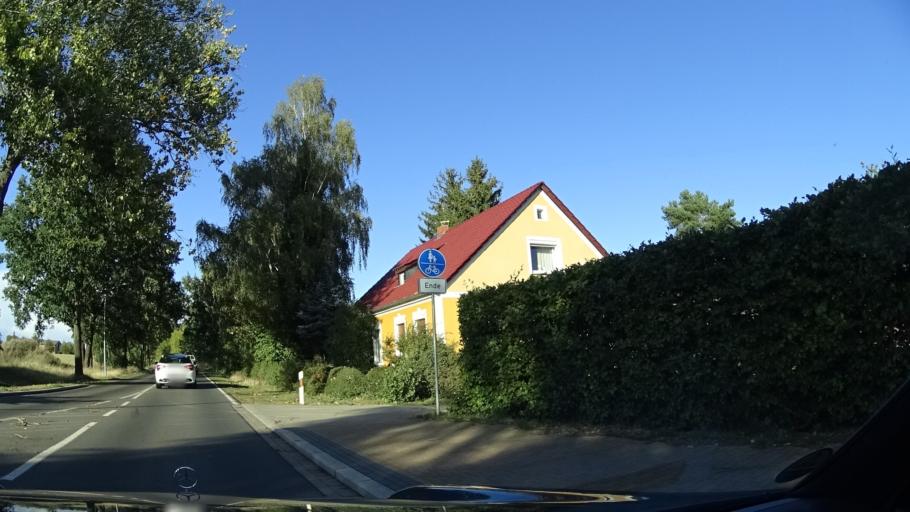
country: DE
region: Brandenburg
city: Neuruppin
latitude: 52.8976
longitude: 12.7992
